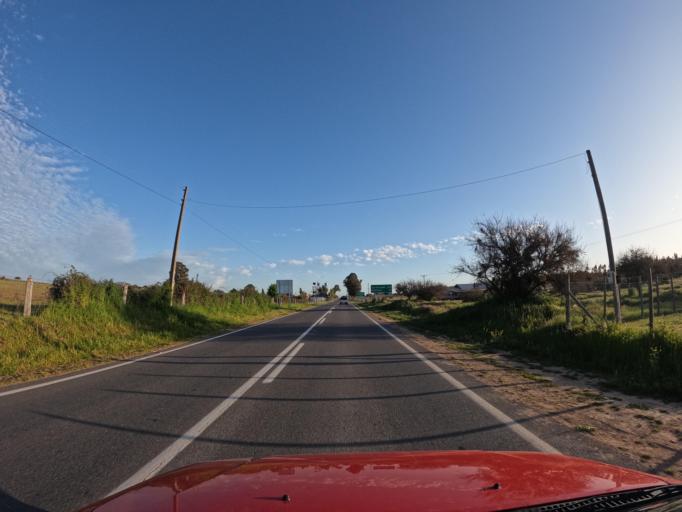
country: CL
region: O'Higgins
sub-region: Provincia de Colchagua
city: Santa Cruz
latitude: -34.2484
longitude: -71.7278
